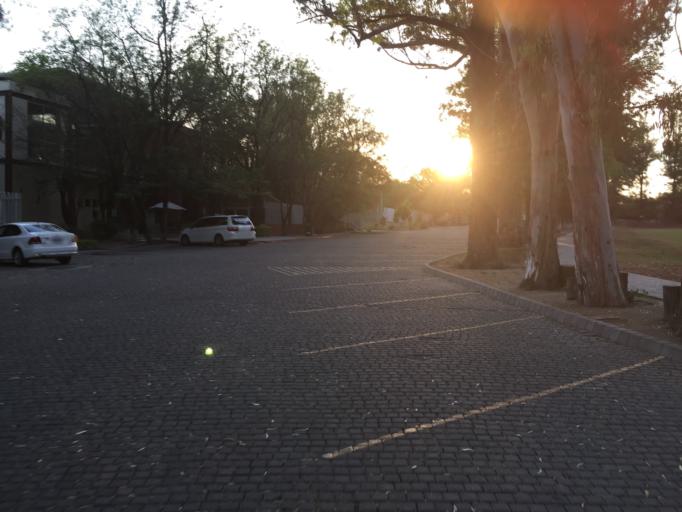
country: MX
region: Aguascalientes
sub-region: Aguascalientes
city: La Loma de los Negritos
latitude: 21.8505
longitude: -102.3573
